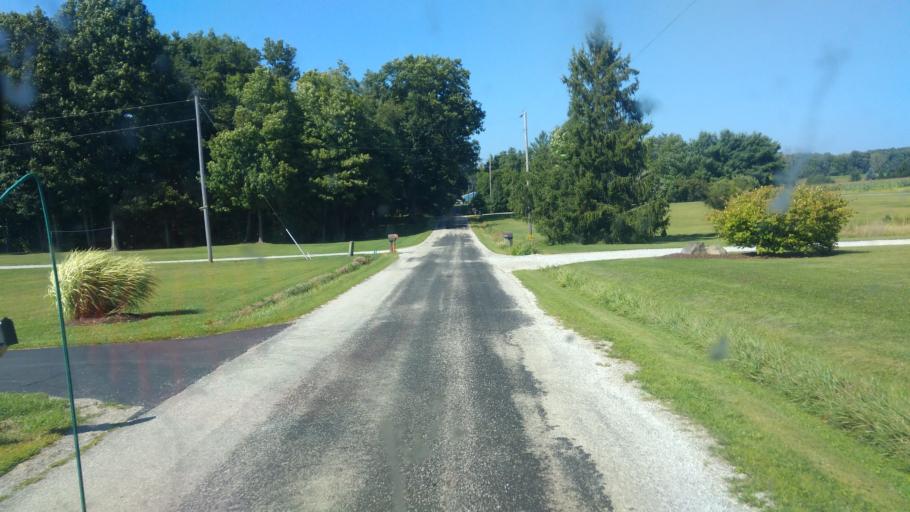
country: US
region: Ohio
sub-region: Ashland County
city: Ashland
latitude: 40.9347
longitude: -82.2626
